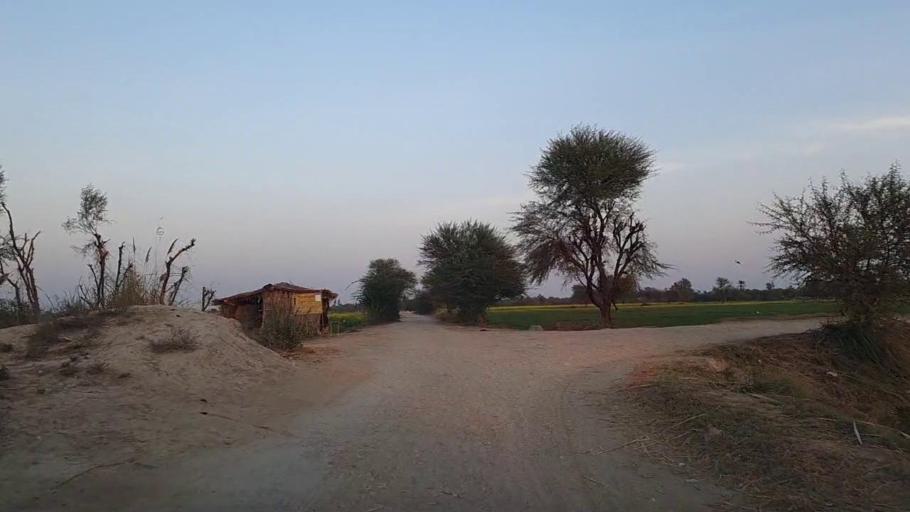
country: PK
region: Sindh
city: Tando Mittha Khan
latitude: 25.9584
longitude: 69.1162
